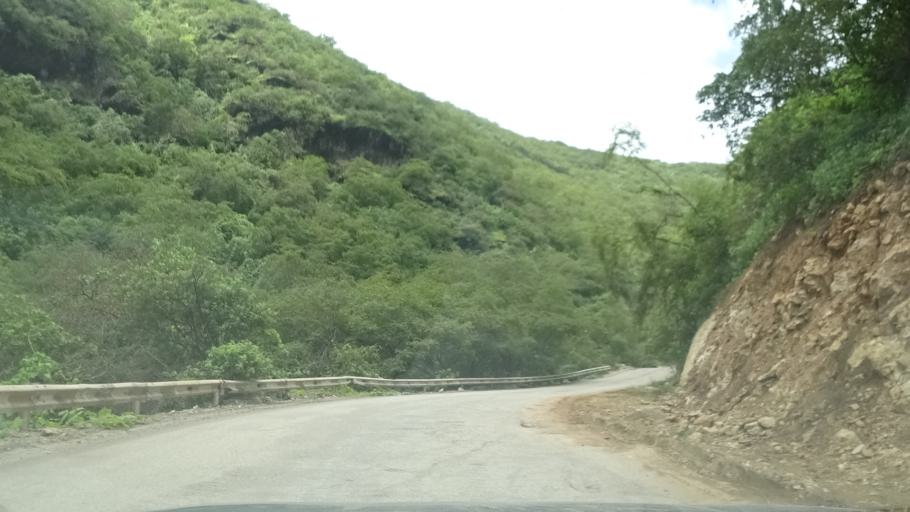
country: OM
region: Zufar
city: Salalah
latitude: 17.1642
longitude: 54.1686
